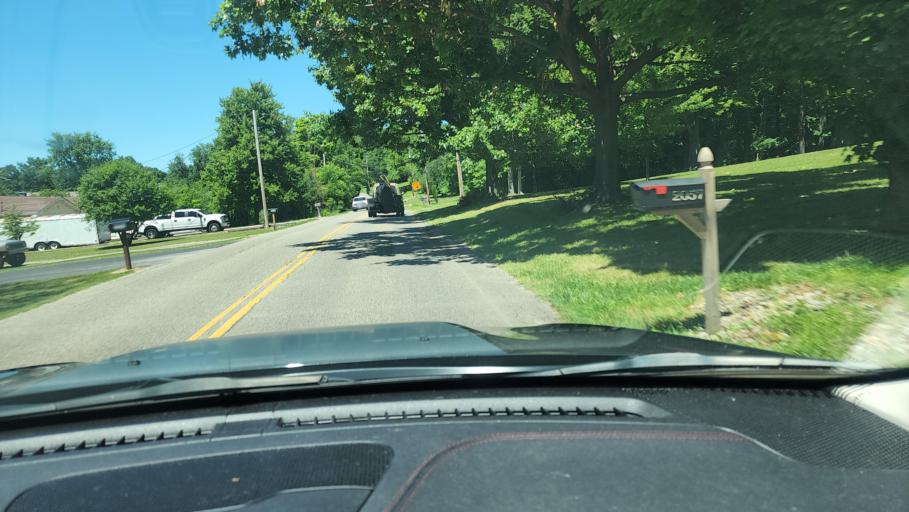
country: US
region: Ohio
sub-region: Mahoning County
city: Austintown
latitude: 41.0801
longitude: -80.7892
